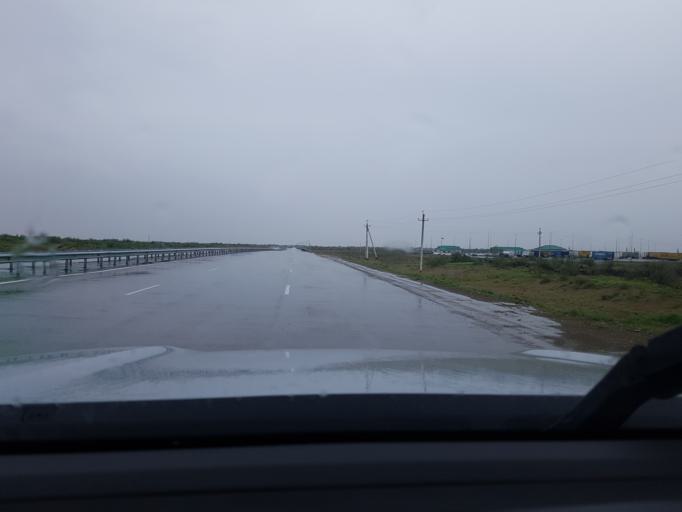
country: TM
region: Lebap
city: Farap
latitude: 39.2079
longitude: 63.6941
